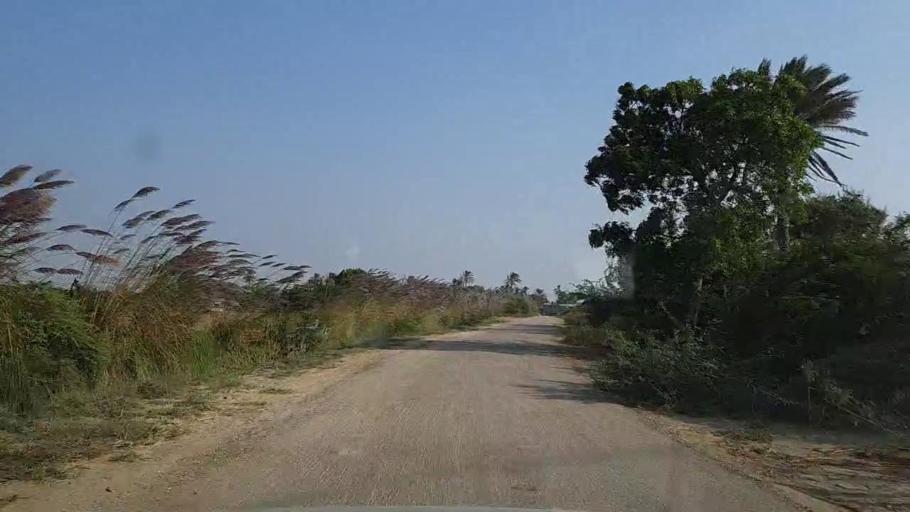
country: PK
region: Sindh
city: Mirpur Sakro
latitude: 24.5941
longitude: 67.6057
